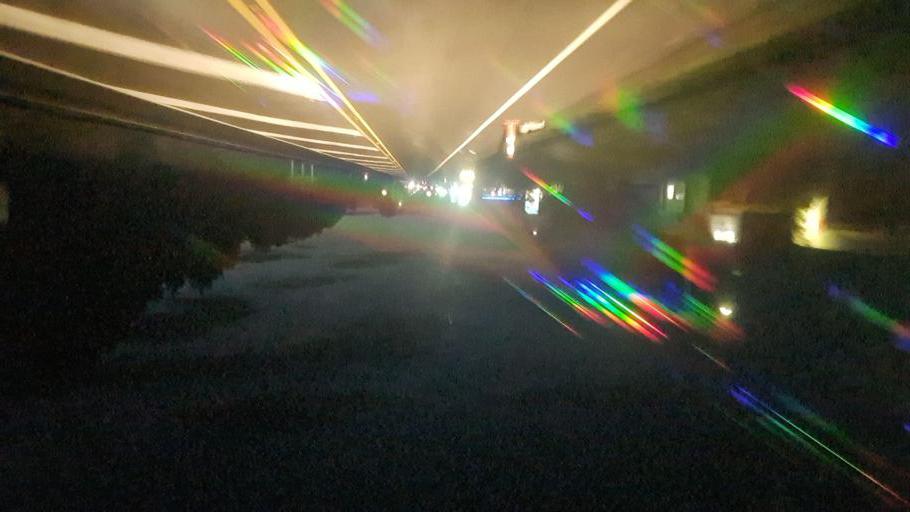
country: NZ
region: Otago
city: Oamaru
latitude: -45.0608
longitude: 171.0007
